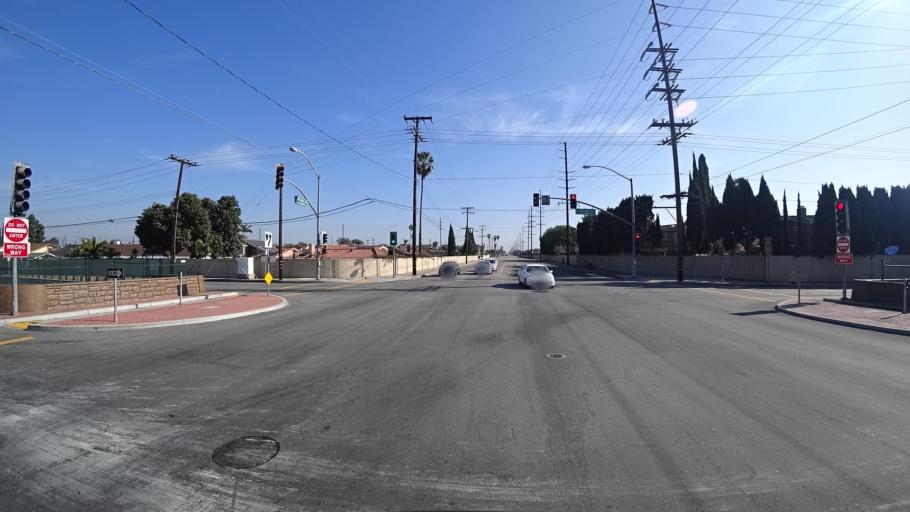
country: US
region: California
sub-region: Orange County
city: Midway City
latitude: 33.7375
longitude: -117.9809
